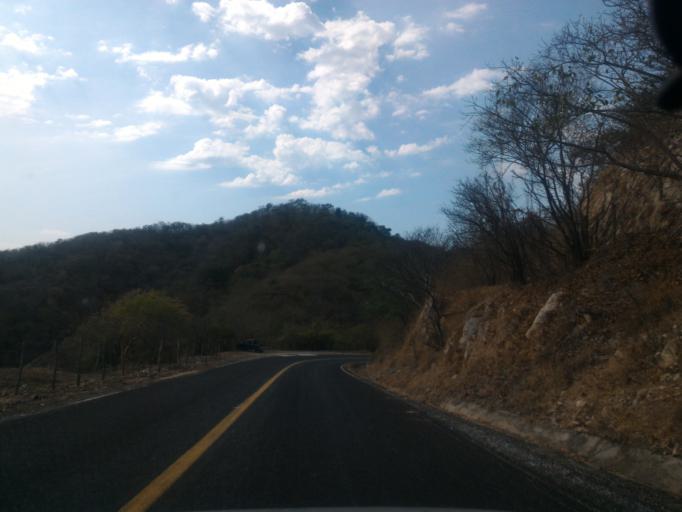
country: MX
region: Michoacan
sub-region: Coalcoman de Vazquez Pallares
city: Coalcoman de Vazquez Pallares
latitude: 18.2824
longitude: -103.3772
